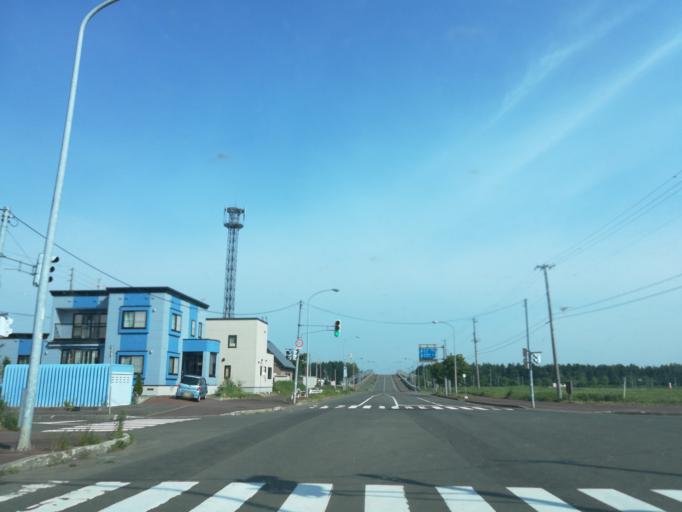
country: JP
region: Hokkaido
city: Iwamizawa
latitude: 43.1746
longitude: 141.7101
